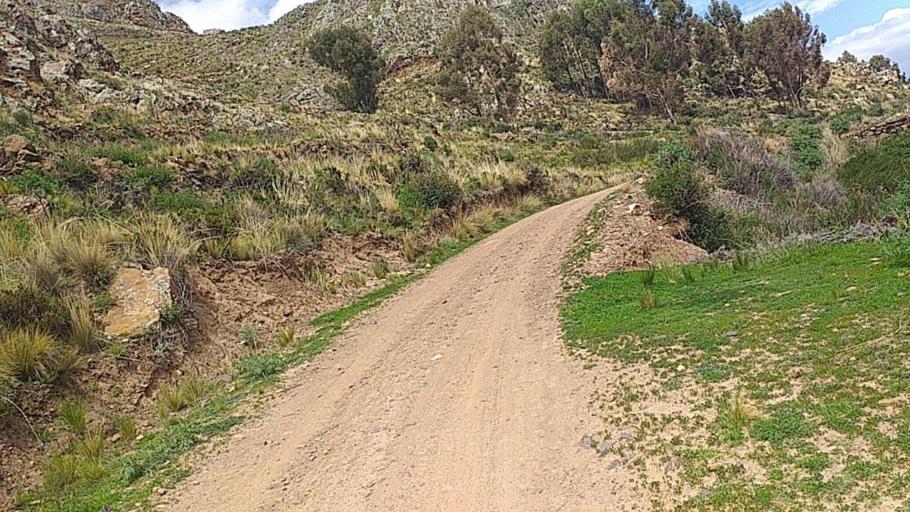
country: BO
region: La Paz
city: Batallas
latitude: -16.3254
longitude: -68.6456
